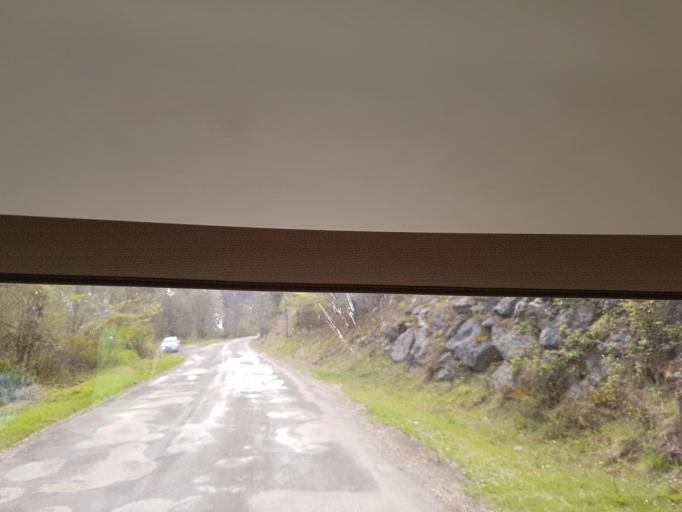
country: FR
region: Languedoc-Roussillon
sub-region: Departement de l'Aude
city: Quillan
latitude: 42.7719
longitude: 2.1268
